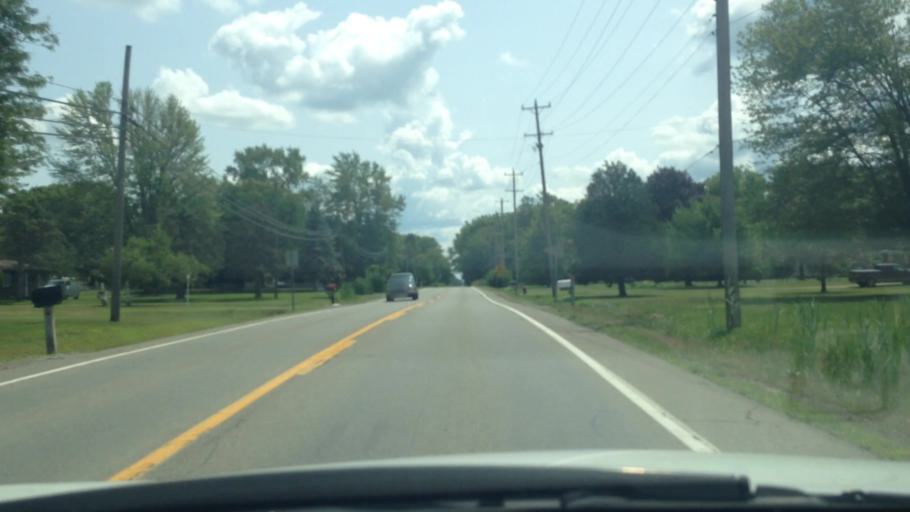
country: US
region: Michigan
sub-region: Wayne County
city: Taylor
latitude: 42.1797
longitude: -83.3060
